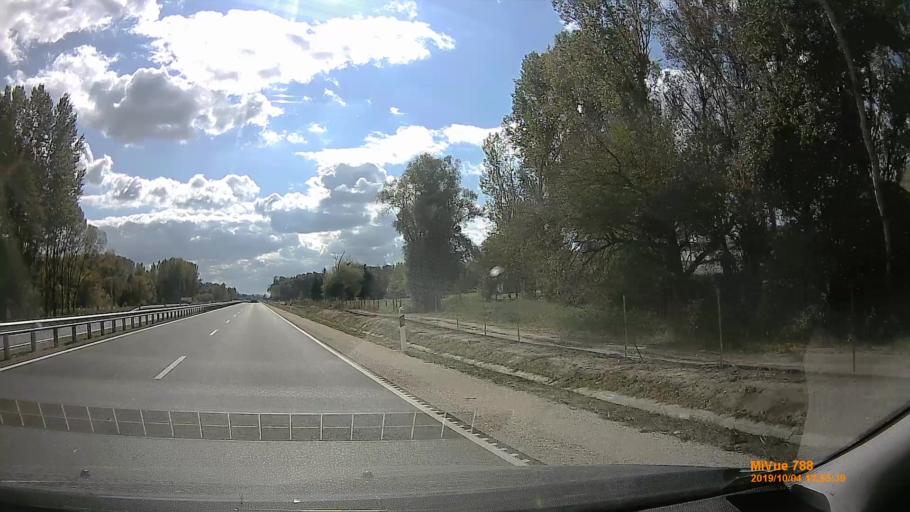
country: HU
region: Somogy
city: Karad
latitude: 46.6797
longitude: 17.7764
